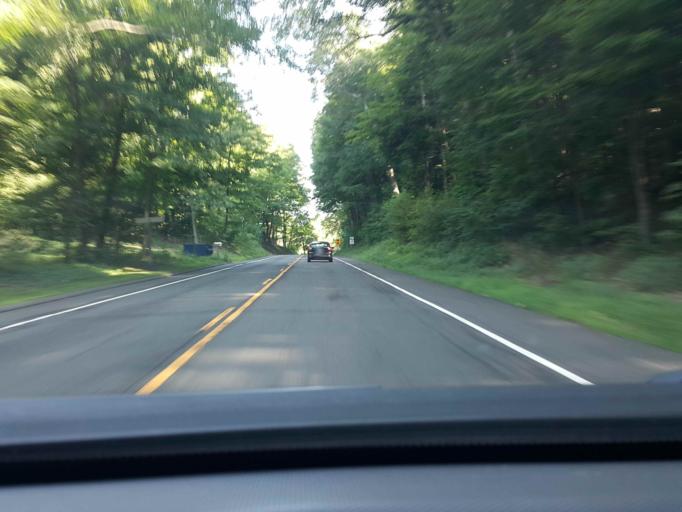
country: US
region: Connecticut
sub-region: Middlesex County
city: Durham
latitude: 41.4605
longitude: -72.6800
